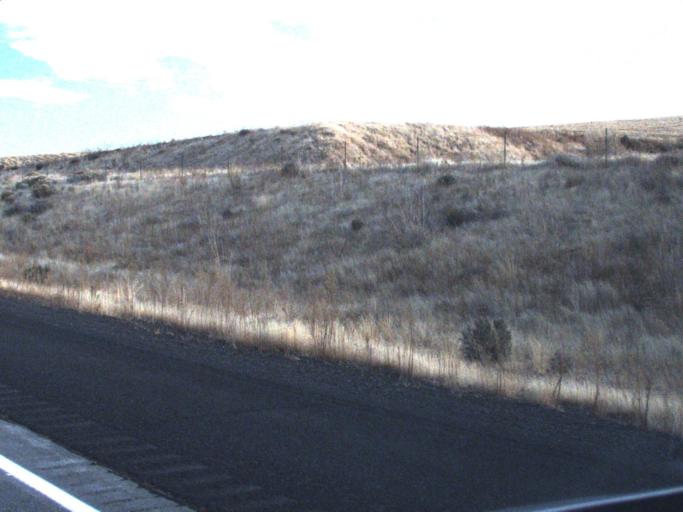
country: US
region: Washington
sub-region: Franklin County
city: Connell
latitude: 46.8619
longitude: -118.6335
